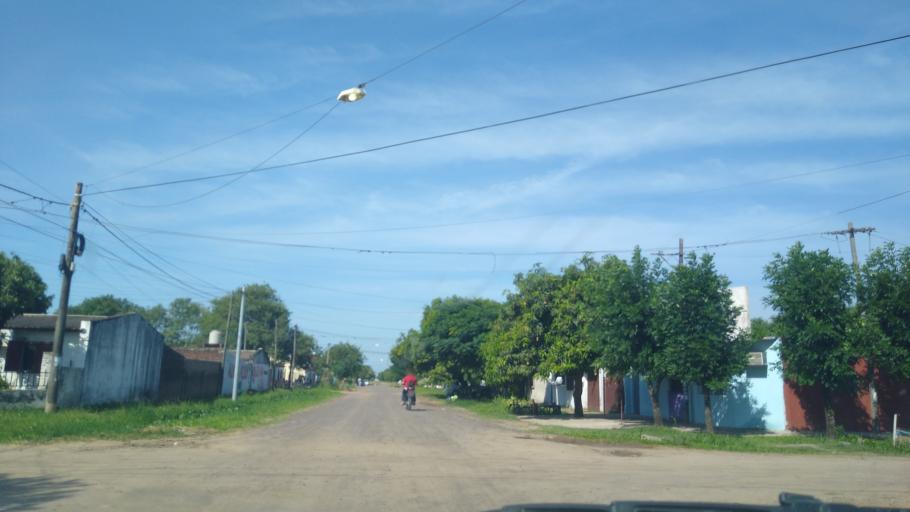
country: AR
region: Chaco
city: Barranqueras
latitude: -27.4926
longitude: -58.9523
